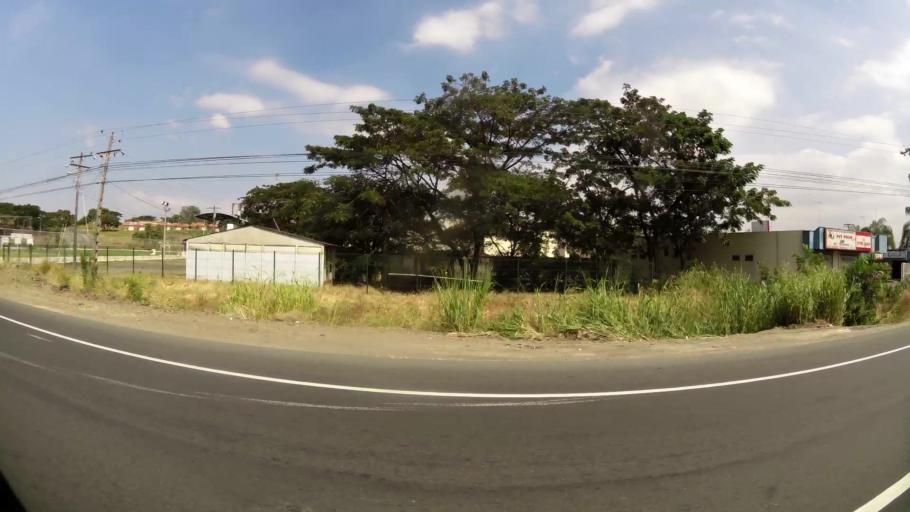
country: EC
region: Guayas
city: El Triunfo
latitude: -2.0487
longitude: -79.9080
